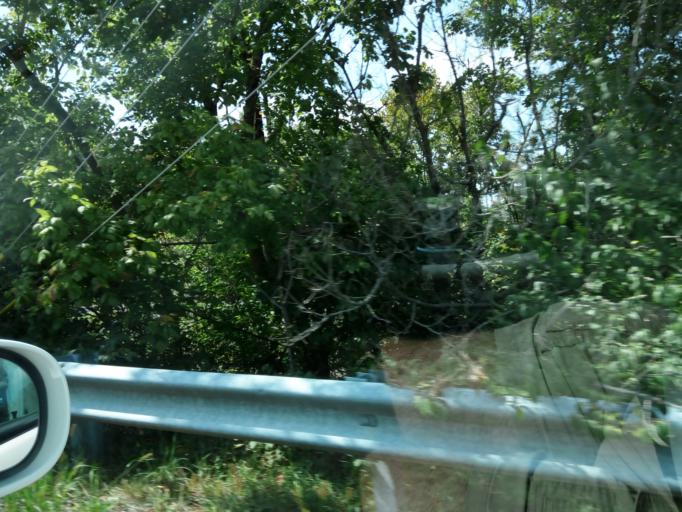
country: US
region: Kentucky
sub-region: Oldham County
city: Pewee Valley
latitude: 38.2414
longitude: -85.4605
